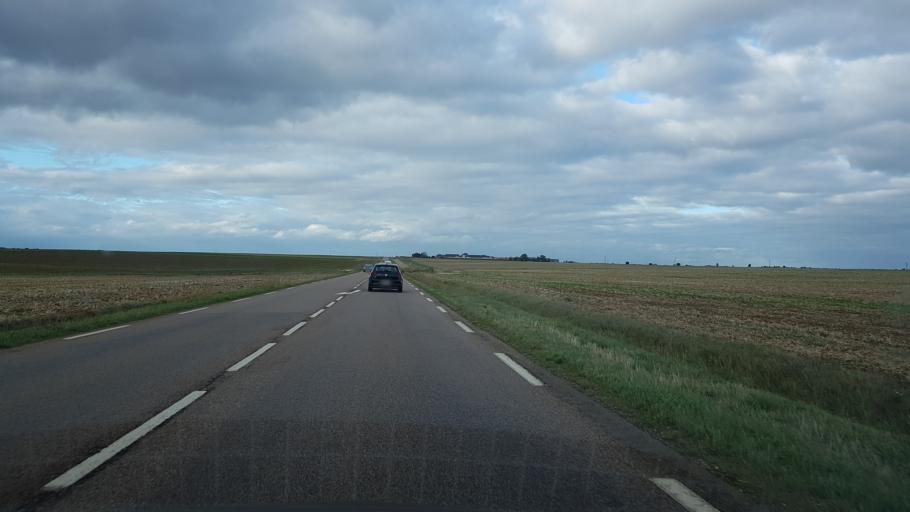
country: FR
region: Ile-de-France
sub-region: Departement de l'Essonne
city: Etampes
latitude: 48.3878
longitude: 2.1705
